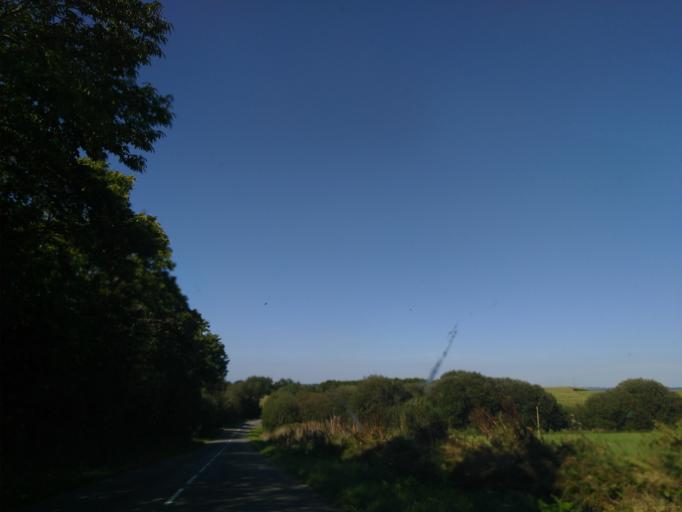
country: FR
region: Brittany
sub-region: Departement du Finistere
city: Le Faou
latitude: 48.2683
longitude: -4.1917
